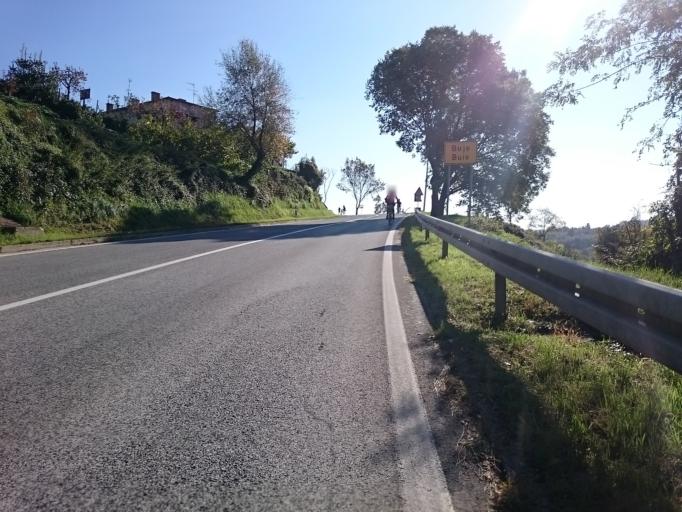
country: HR
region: Istarska
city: Buje
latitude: 45.4086
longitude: 13.6556
